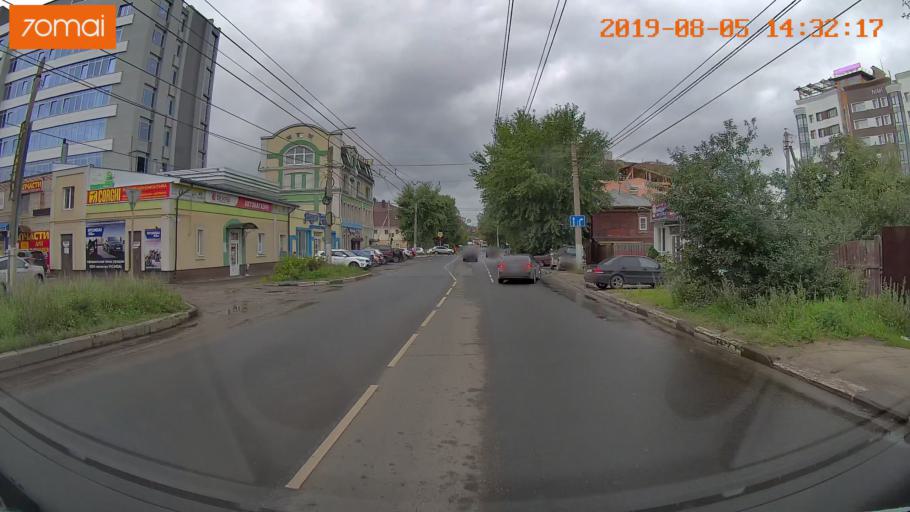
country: RU
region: Ivanovo
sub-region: Gorod Ivanovo
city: Ivanovo
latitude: 56.9907
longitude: 40.9911
